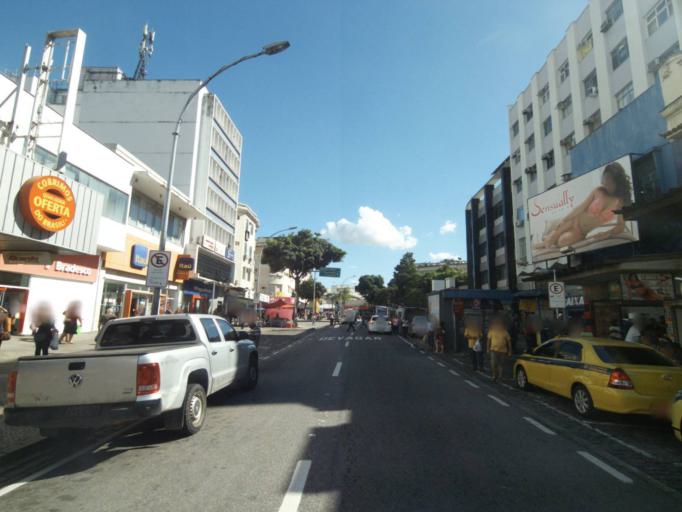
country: BR
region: Rio de Janeiro
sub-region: Rio De Janeiro
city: Rio de Janeiro
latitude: -22.9021
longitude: -43.2786
